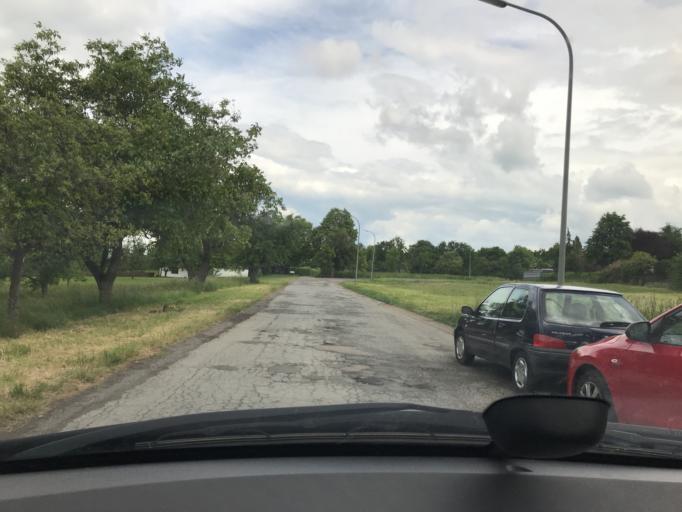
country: DE
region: Saarland
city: Kleinblittersdorf
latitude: 49.1644
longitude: 7.0392
